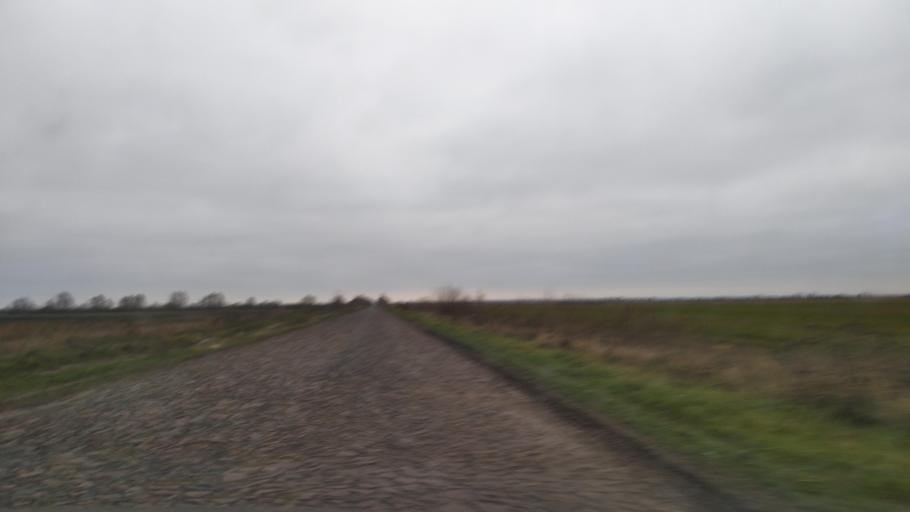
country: BY
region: Brest
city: Davyd-Haradok
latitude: 52.0078
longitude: 27.2055
